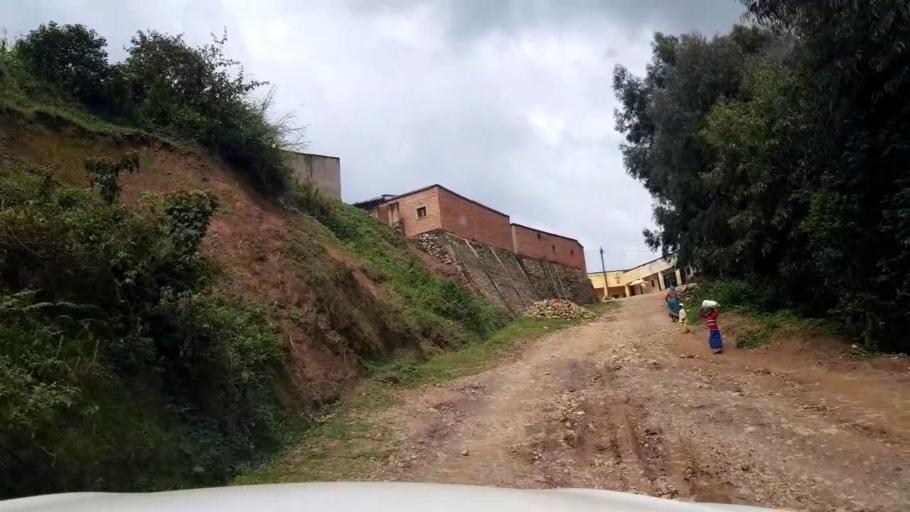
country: RW
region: Western Province
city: Kibuye
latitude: -1.8940
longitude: 29.4569
